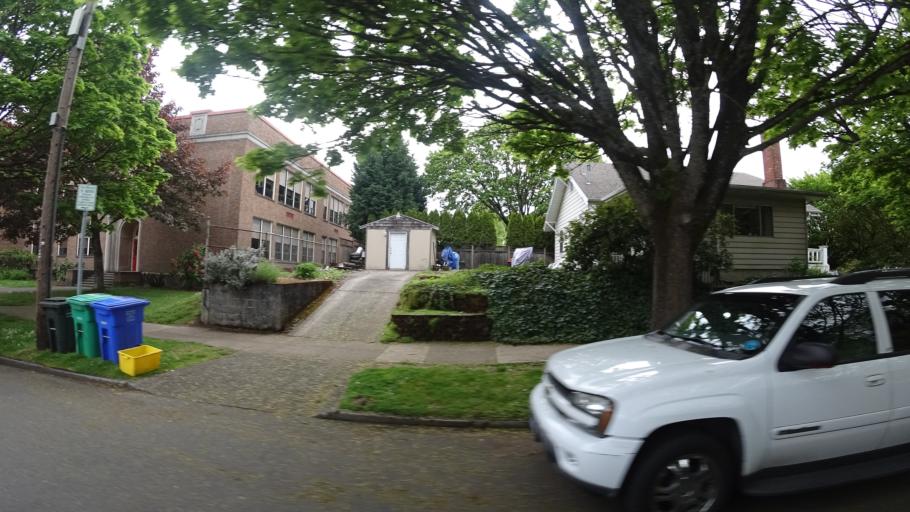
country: US
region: Oregon
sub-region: Clackamas County
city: Milwaukie
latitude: 45.4775
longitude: -122.6518
